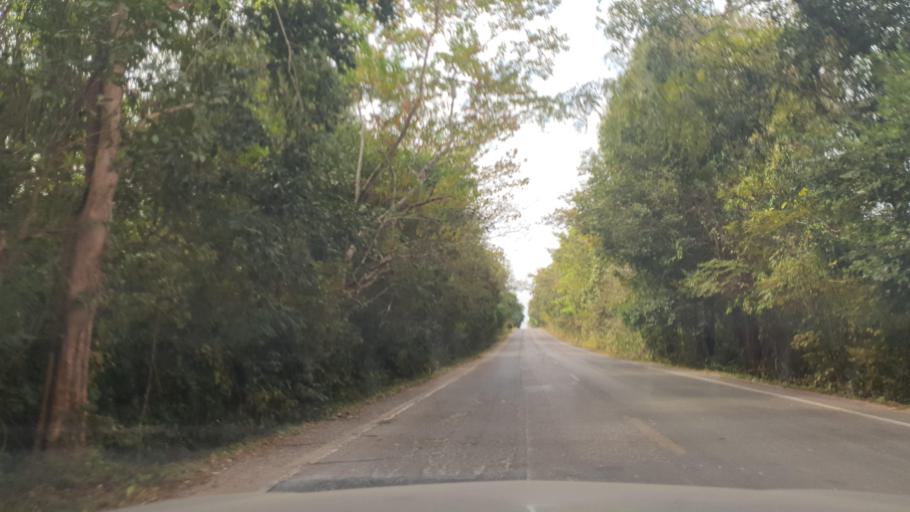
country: TH
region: Changwat Bueng Kan
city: Bung Khla
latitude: 18.2954
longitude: 103.9293
